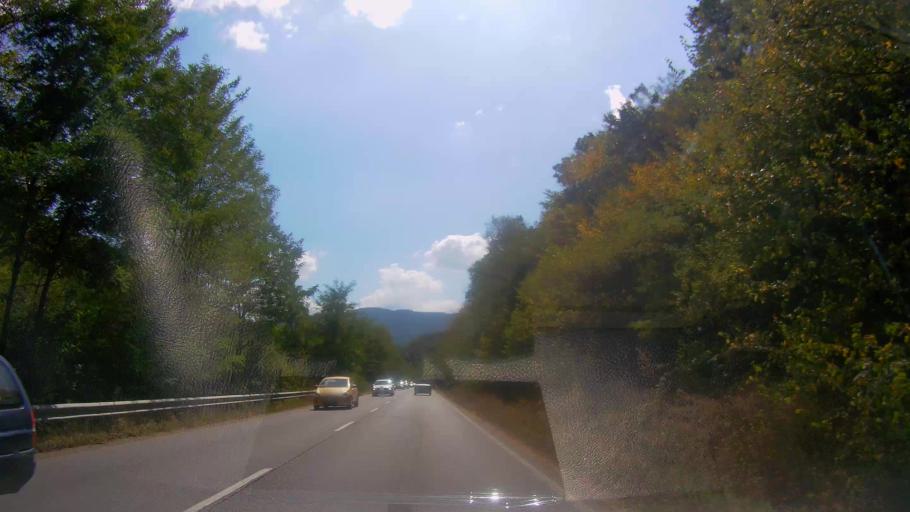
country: BG
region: Stara Zagora
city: Gurkovo
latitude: 42.7296
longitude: 25.7122
